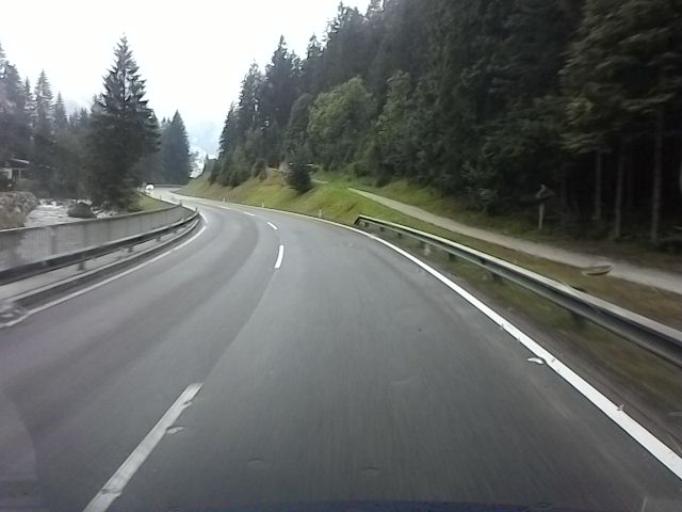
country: AT
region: Tyrol
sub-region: Politischer Bezirk Reutte
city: Ehrwald
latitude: 47.4127
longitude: 10.9134
